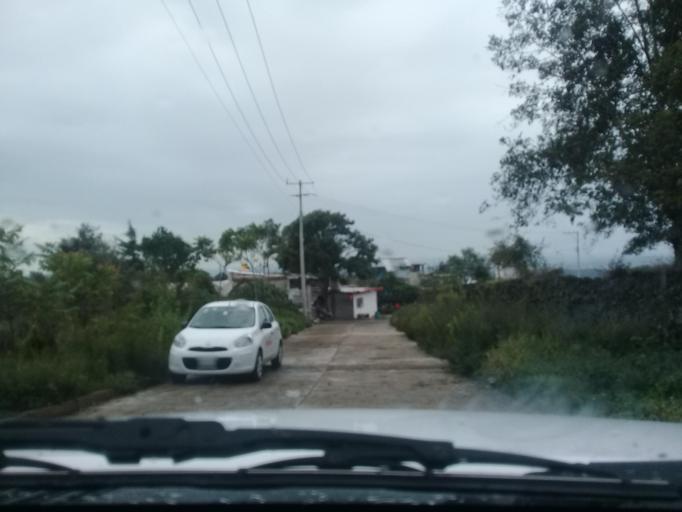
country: MX
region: Veracruz
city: Rafael Lucio
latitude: 19.6163
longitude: -96.9933
